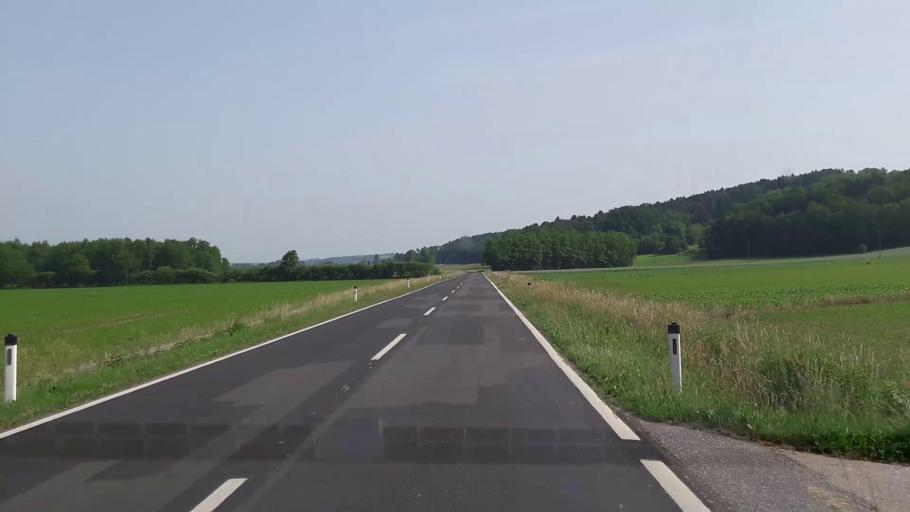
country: AT
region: Burgenland
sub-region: Politischer Bezirk Jennersdorf
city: Deutsch Kaltenbrunn
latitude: 47.1035
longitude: 16.1096
